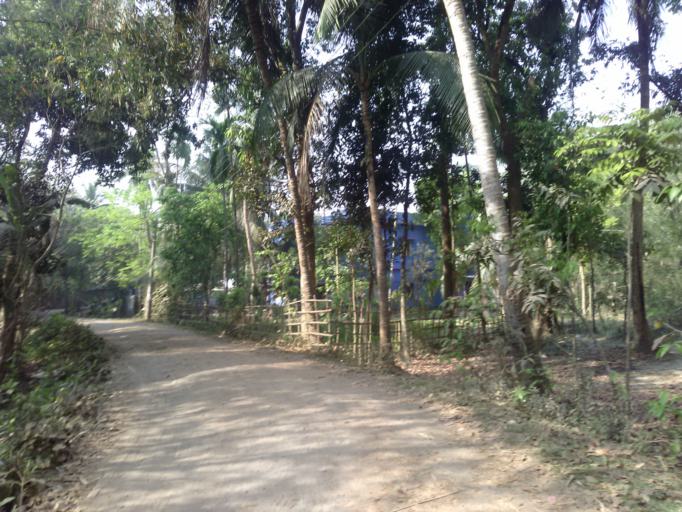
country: BD
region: Khulna
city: Khulna
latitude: 22.8976
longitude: 89.5273
